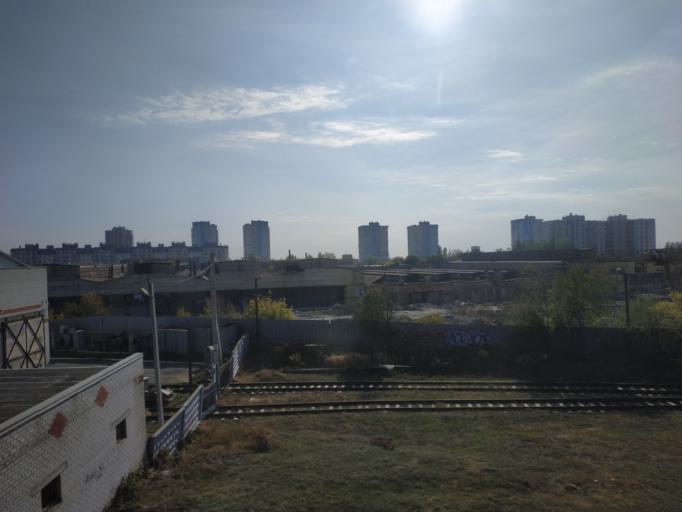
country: RU
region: Volgograd
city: Volgograd
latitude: 48.7343
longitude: 44.5380
